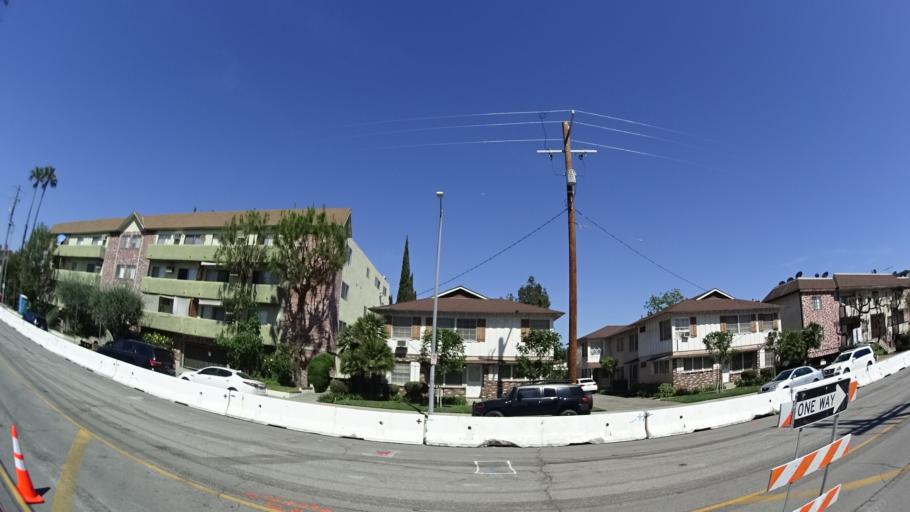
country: US
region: California
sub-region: Los Angeles County
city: North Hollywood
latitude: 34.1772
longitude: -118.4053
